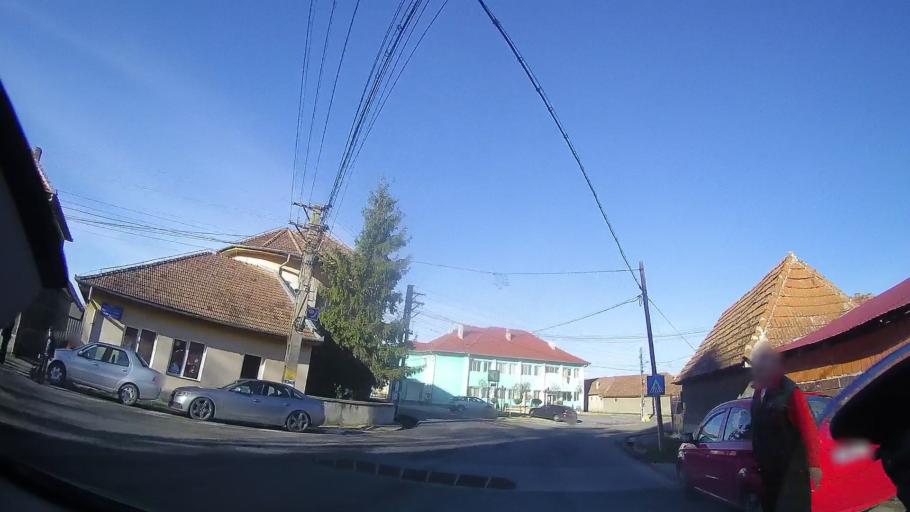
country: RO
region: Bihor
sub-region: Comuna Vadu Crisului
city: Vadu Crisului
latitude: 46.9869
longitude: 22.5133
